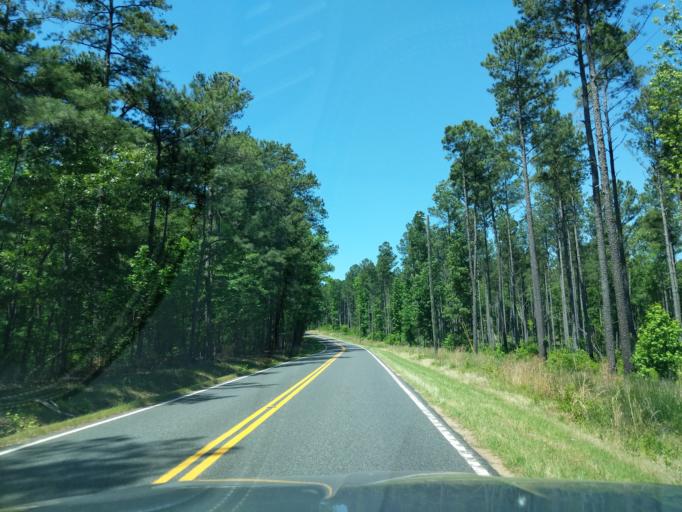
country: US
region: Georgia
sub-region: Columbia County
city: Evans
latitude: 33.6242
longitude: -82.1170
